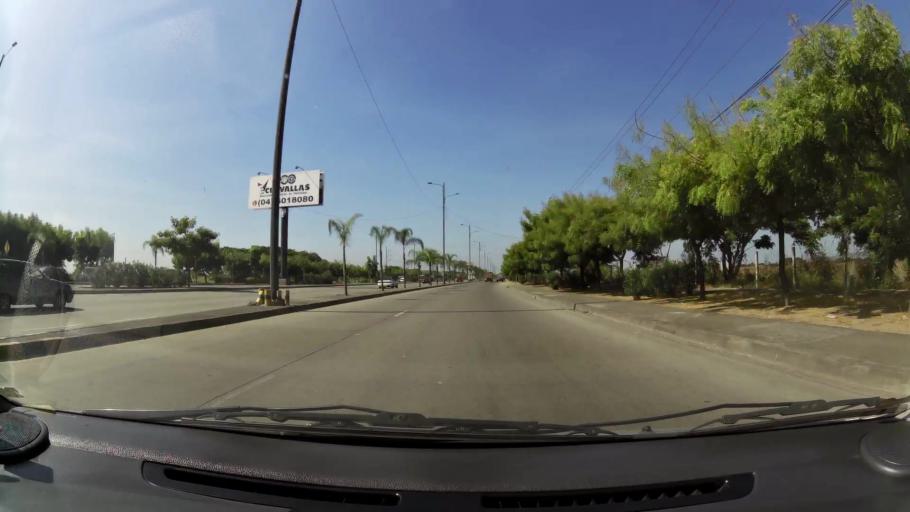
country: EC
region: Guayas
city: Eloy Alfaro
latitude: -2.1008
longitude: -79.8897
